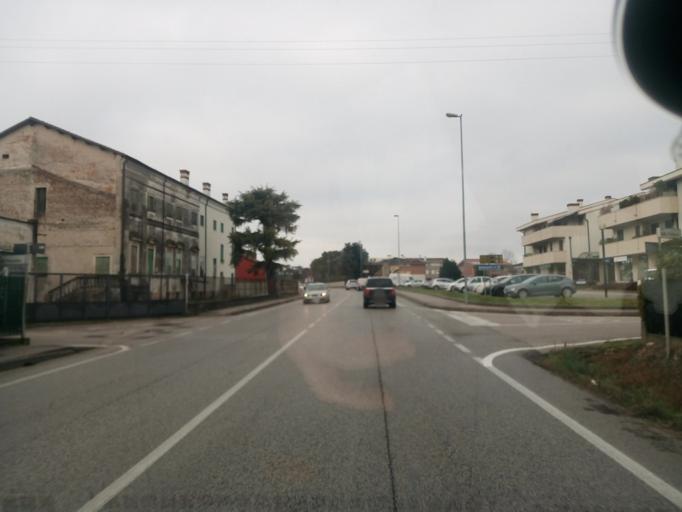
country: IT
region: Veneto
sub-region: Provincia di Vicenza
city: Sandrigo
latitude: 45.6623
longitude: 11.6056
